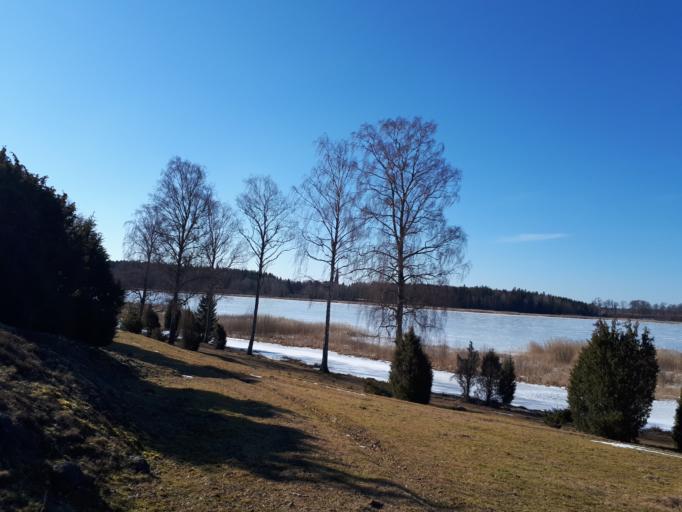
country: SE
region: Soedermanland
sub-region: Flens Kommun
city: Halleforsnas
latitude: 59.0778
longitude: 16.3710
